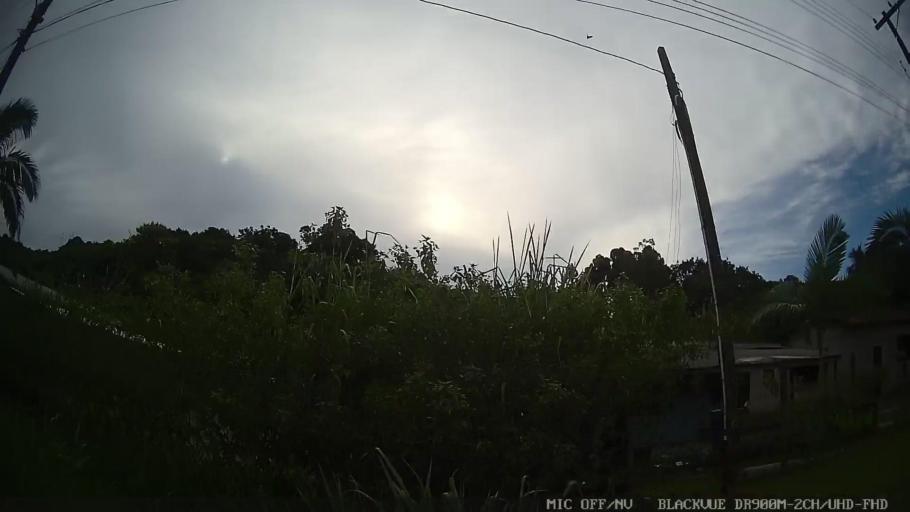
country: BR
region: Sao Paulo
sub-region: Iguape
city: Iguape
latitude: -24.6595
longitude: -47.4145
